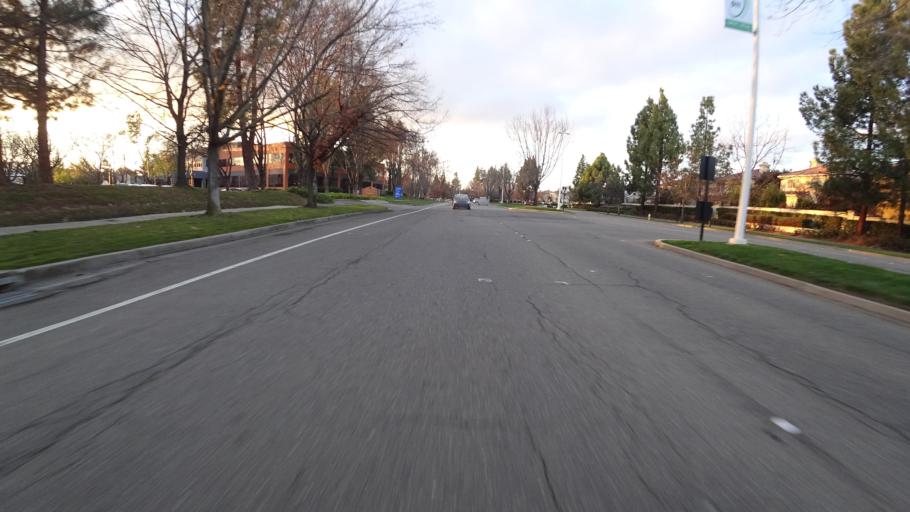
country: US
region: California
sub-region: Alameda County
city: Pleasanton
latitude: 37.6910
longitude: -121.8884
